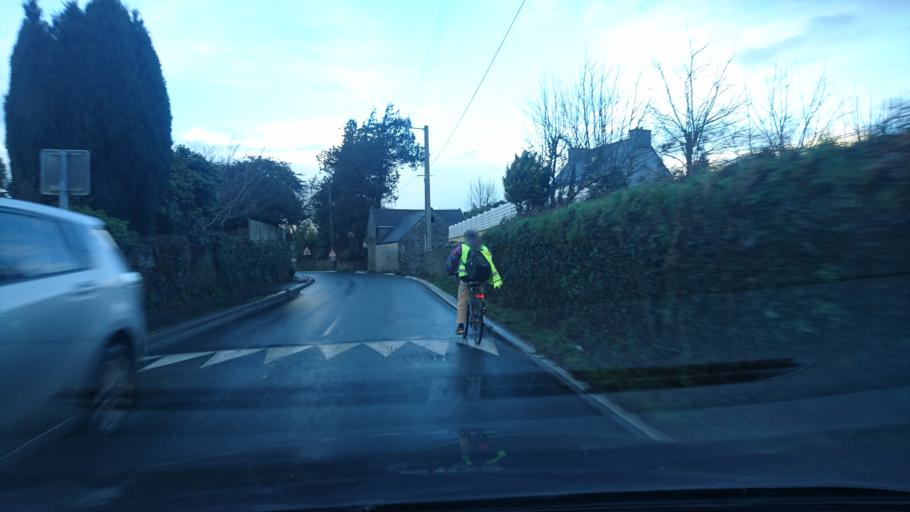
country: FR
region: Brittany
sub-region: Departement du Finistere
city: Guilers
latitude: 48.3979
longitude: -4.5394
